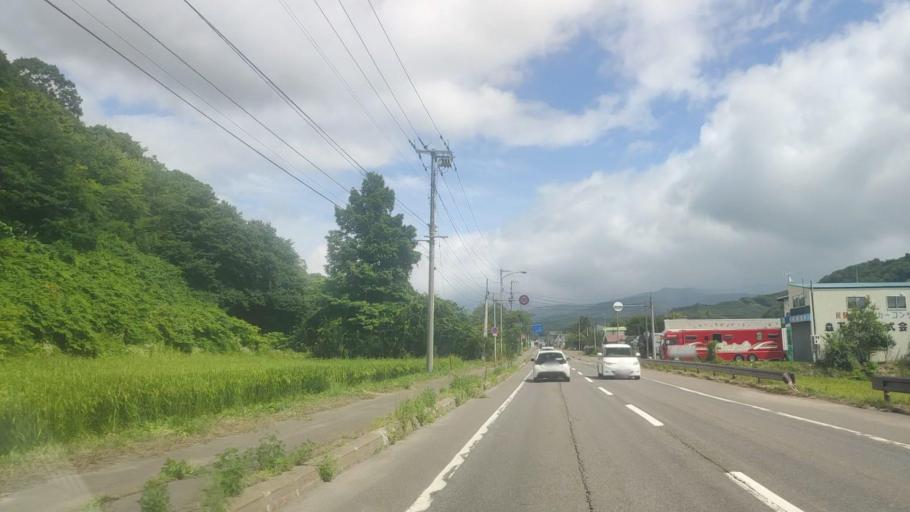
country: JP
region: Hokkaido
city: Date
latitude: 42.5790
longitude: 140.9511
